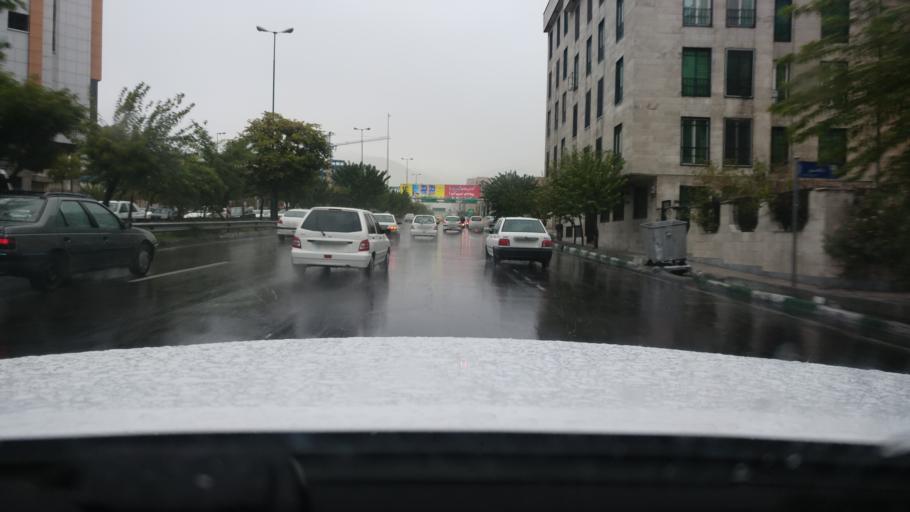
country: IR
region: Tehran
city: Tehran
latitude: 35.7242
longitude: 51.3092
